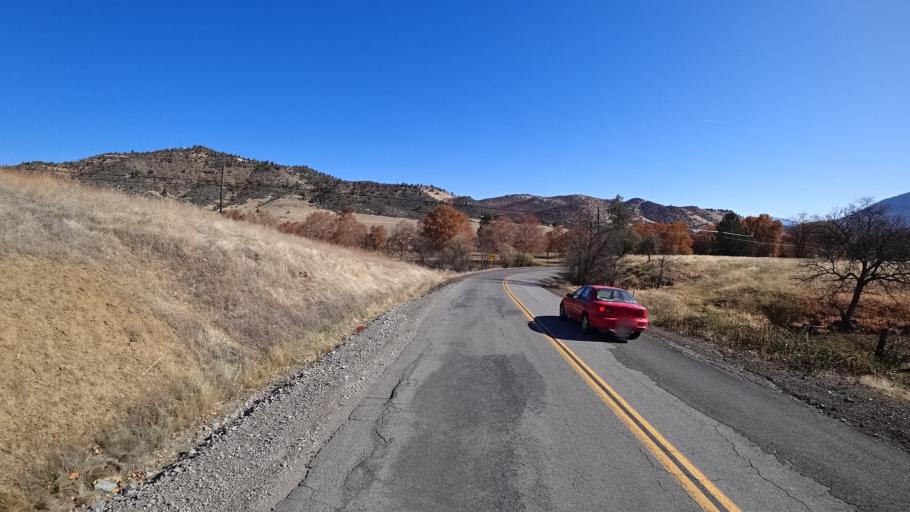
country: US
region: California
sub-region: Siskiyou County
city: Yreka
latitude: 41.9202
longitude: -122.5688
